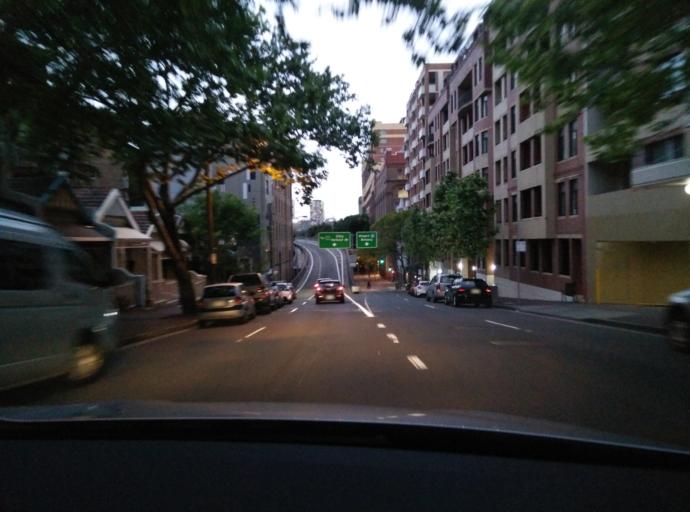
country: AU
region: New South Wales
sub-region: City of Sydney
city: Haymarket
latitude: -33.8720
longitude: 151.1964
